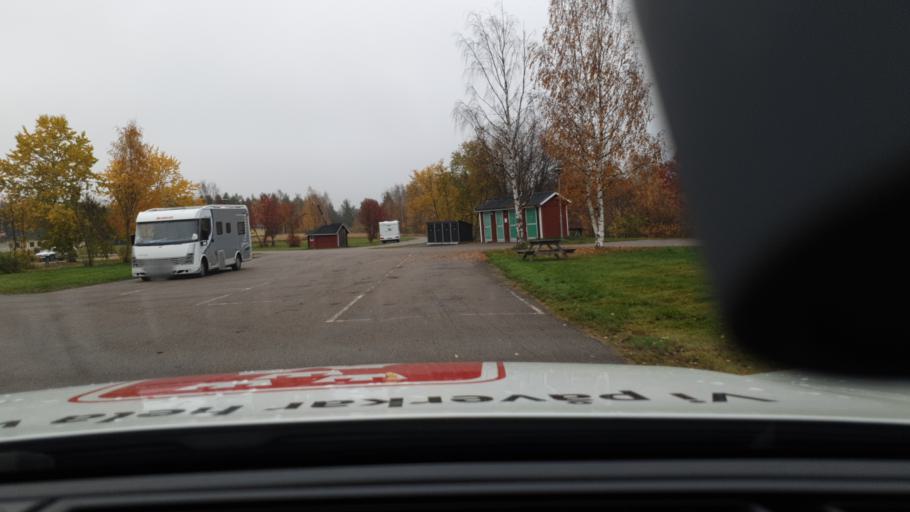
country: SE
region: Norrbotten
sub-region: Overkalix Kommun
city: OEverkalix
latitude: 66.6499
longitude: 22.1838
